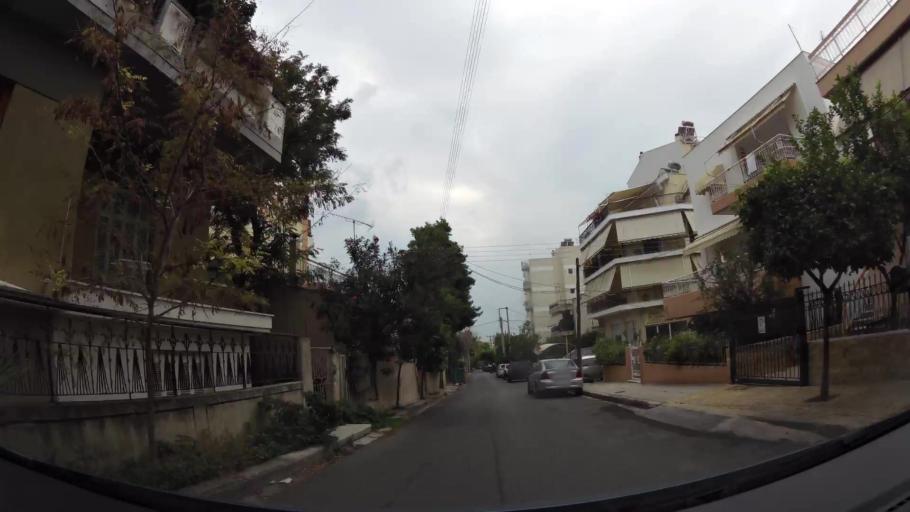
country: GR
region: Attica
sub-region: Nomarchia Athinas
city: Agios Dimitrios
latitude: 37.9289
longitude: 23.7197
